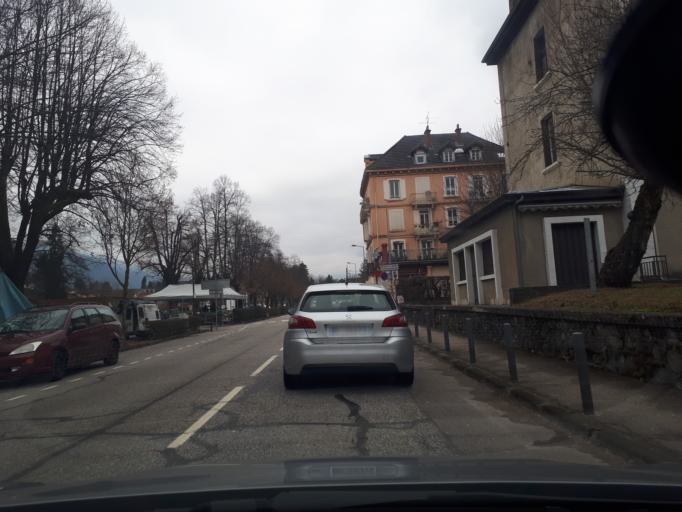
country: FR
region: Rhone-Alpes
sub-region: Departement de l'Isere
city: Vaulnaveys-le-Haut
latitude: 45.1383
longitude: 5.8262
